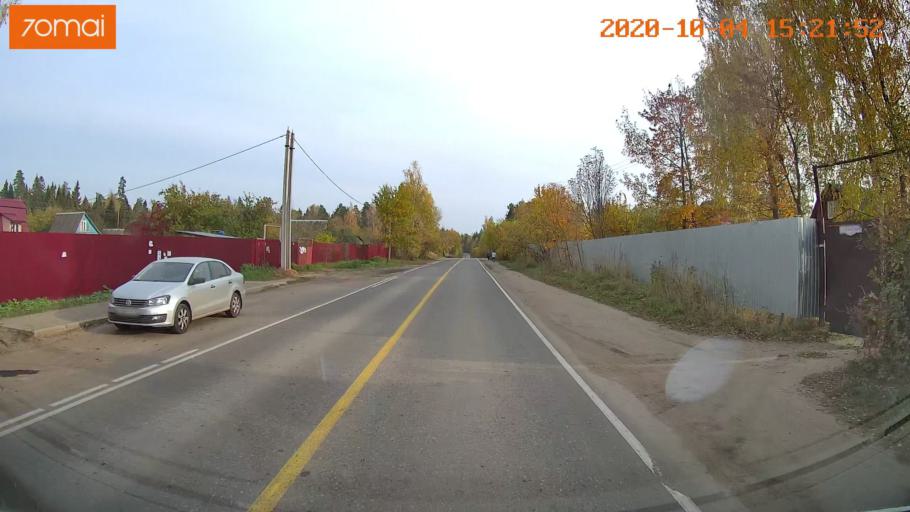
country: RU
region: Ivanovo
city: Bogorodskoye
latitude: 57.0839
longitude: 40.9276
